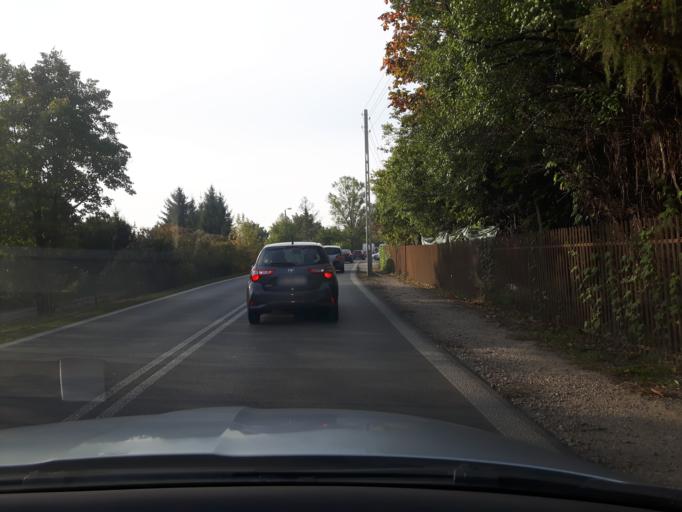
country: PL
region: Masovian Voivodeship
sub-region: Powiat wolominski
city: Zabki
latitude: 52.2812
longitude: 21.0962
